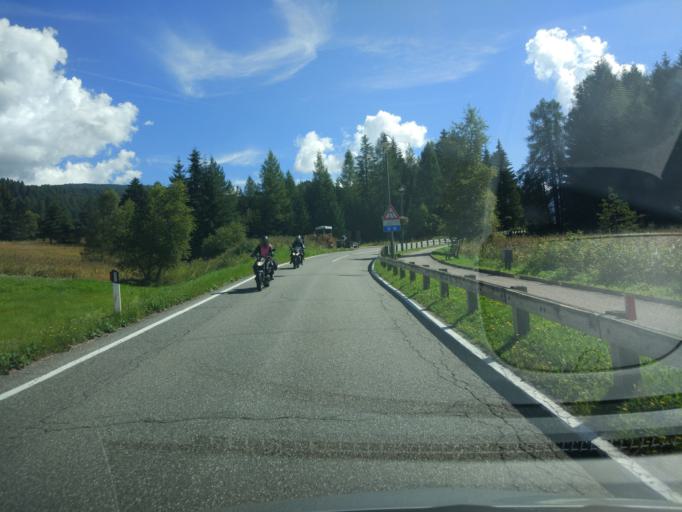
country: IT
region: Trentino-Alto Adige
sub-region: Provincia di Trento
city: Moena
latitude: 46.3122
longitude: 11.6687
